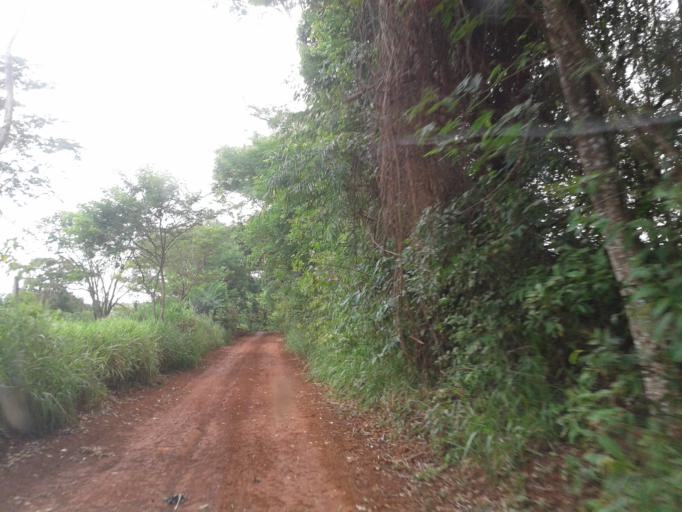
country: BR
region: Minas Gerais
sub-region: Centralina
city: Centralina
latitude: -18.6528
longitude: -49.3410
